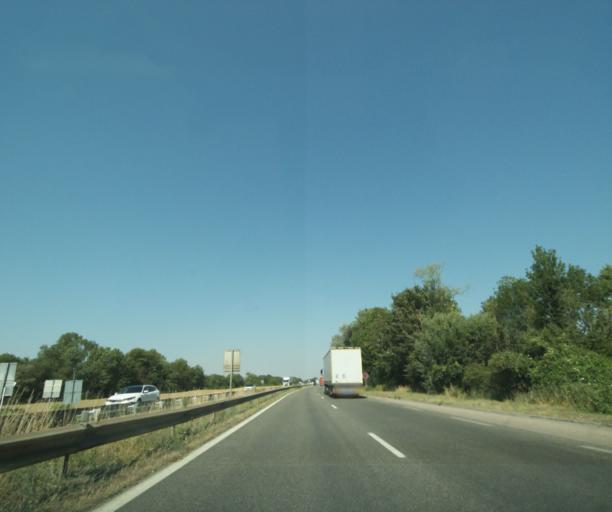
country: FR
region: Champagne-Ardenne
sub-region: Departement de la Haute-Marne
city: Villiers-en-Lieu
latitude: 48.6423
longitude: 4.9015
